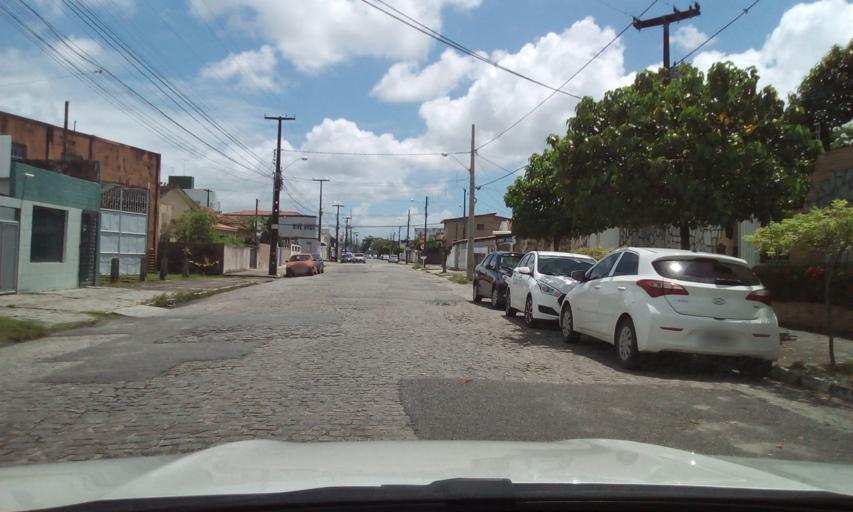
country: BR
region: Paraiba
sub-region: Joao Pessoa
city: Joao Pessoa
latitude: -7.1369
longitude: -34.8775
